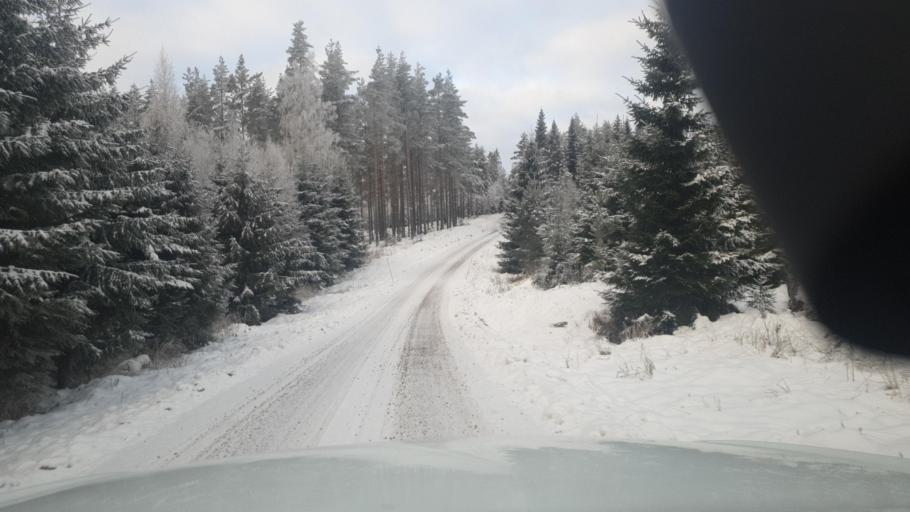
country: SE
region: Vaermland
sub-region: Torsby Kommun
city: Torsby
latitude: 59.9476
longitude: 12.7916
